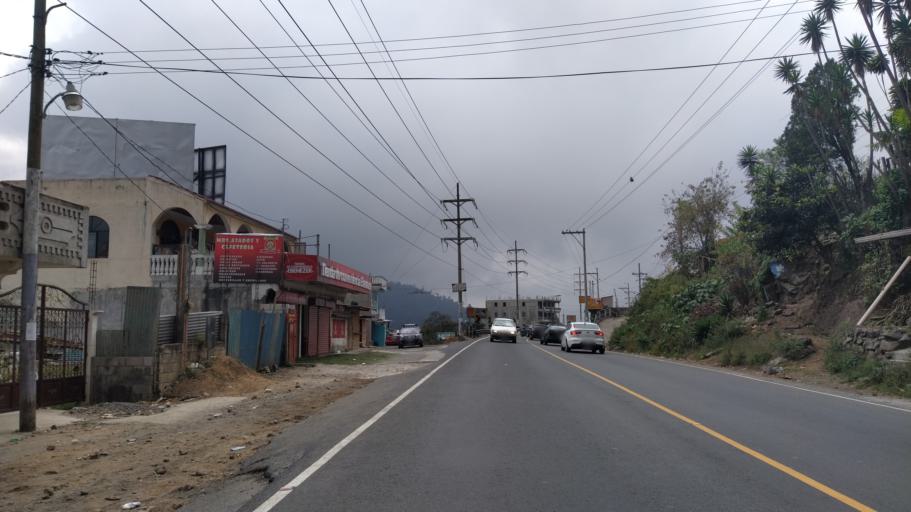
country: GT
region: Quetzaltenango
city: Zunil
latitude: 14.7493
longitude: -91.5103
